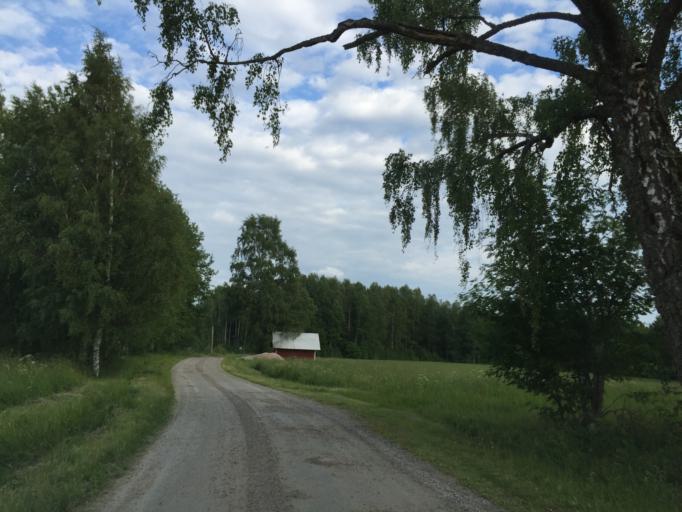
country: SE
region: OErebro
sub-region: Lindesbergs Kommun
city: Fellingsbro
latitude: 59.3263
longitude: 15.5318
